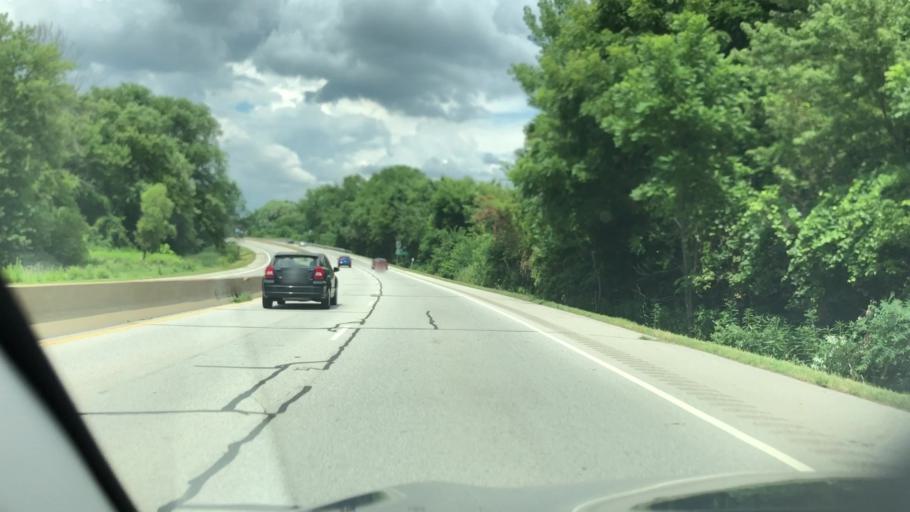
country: US
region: Ohio
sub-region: Stark County
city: Massillon
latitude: 40.8074
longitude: -81.5256
